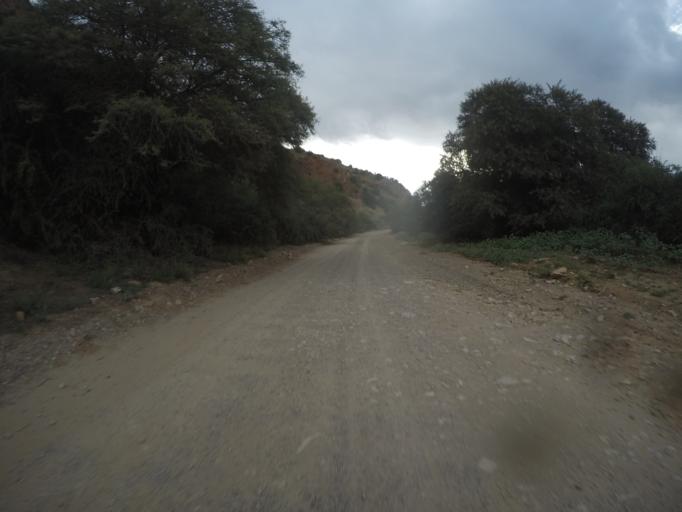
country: ZA
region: Eastern Cape
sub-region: Cacadu District Municipality
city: Willowmore
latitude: -33.5250
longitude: 23.8449
